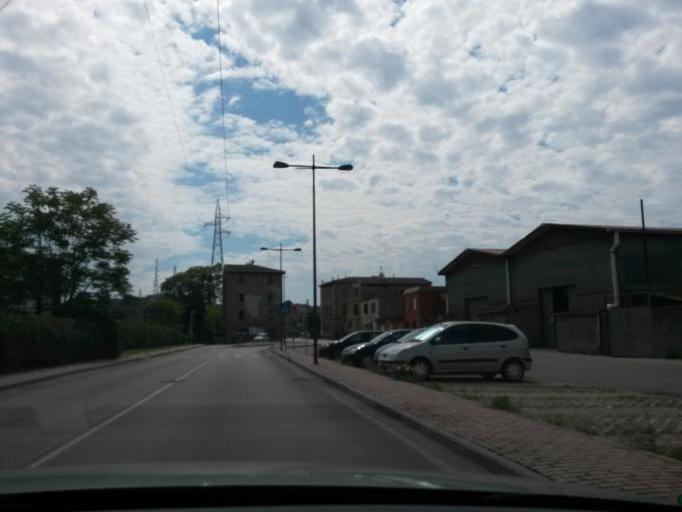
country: IT
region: Tuscany
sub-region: Provincia di Livorno
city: Piombino
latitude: 42.9275
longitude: 10.5336
